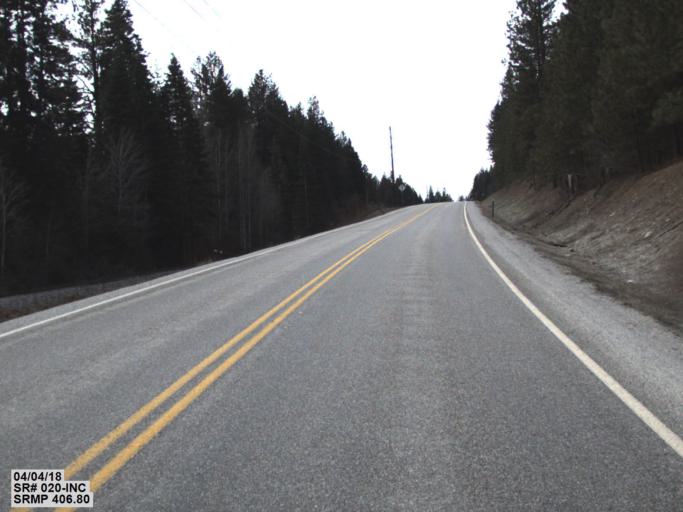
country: US
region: Washington
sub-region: Pend Oreille County
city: Newport
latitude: 48.4861
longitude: -117.2698
